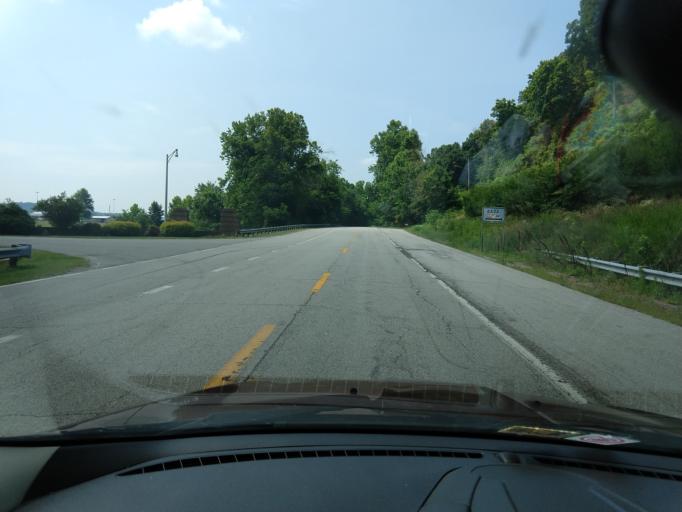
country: US
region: West Virginia
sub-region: Mason County
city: New Haven
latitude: 38.9223
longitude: -81.9138
